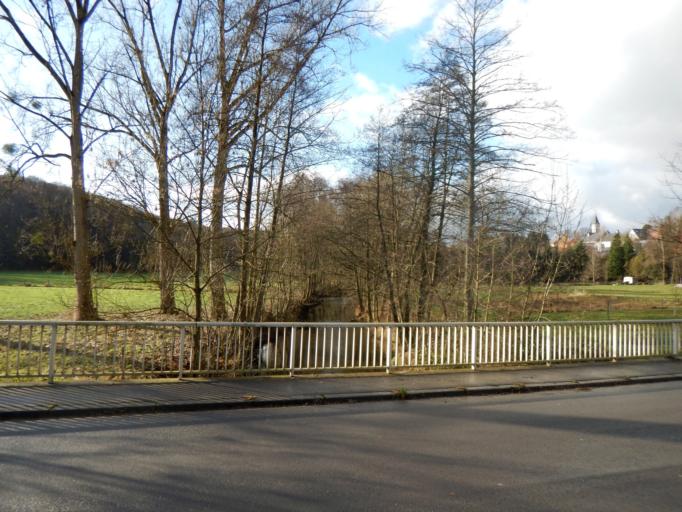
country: LU
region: Diekirch
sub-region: Canton de Redange
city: Redange-sur-Attert
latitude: 49.7632
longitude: 5.8948
